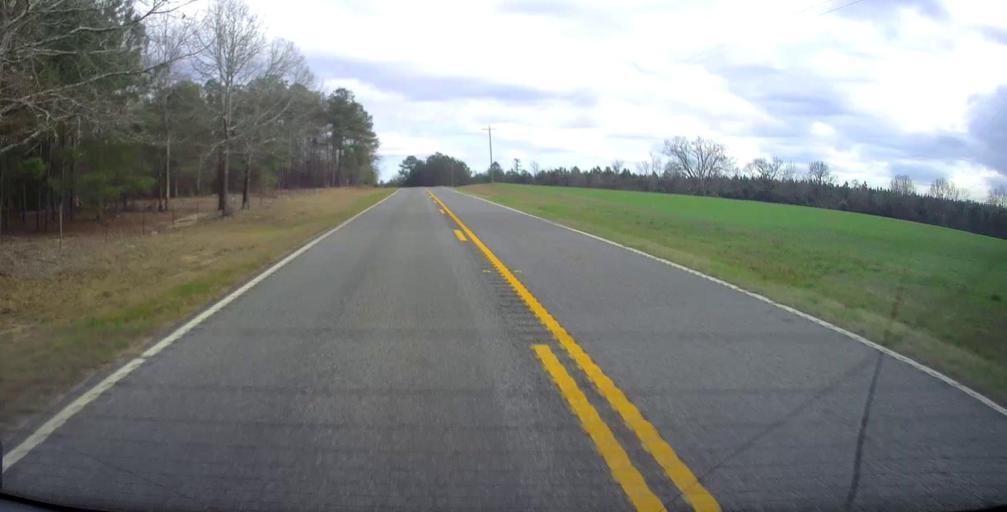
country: US
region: Georgia
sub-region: Marion County
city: Buena Vista
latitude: 32.4375
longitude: -84.4343
